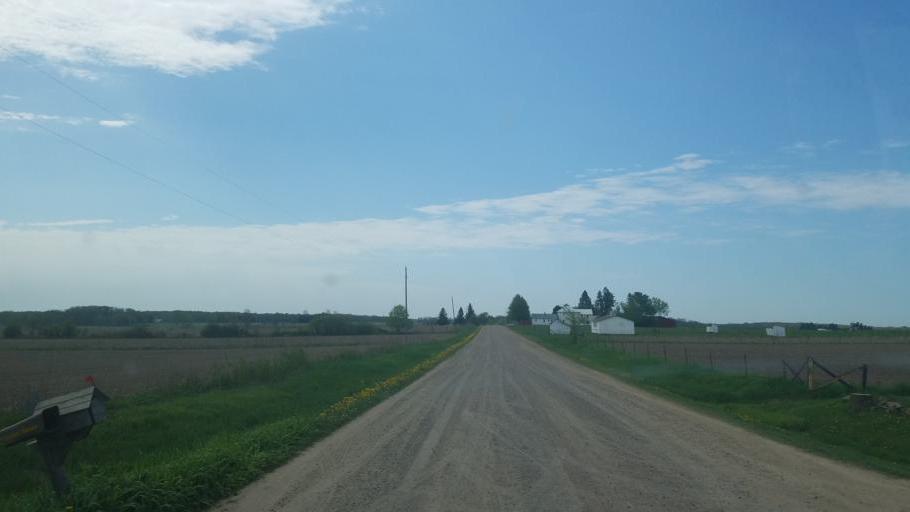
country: US
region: Wisconsin
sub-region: Marathon County
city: Spencer
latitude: 44.6388
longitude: -90.3771
